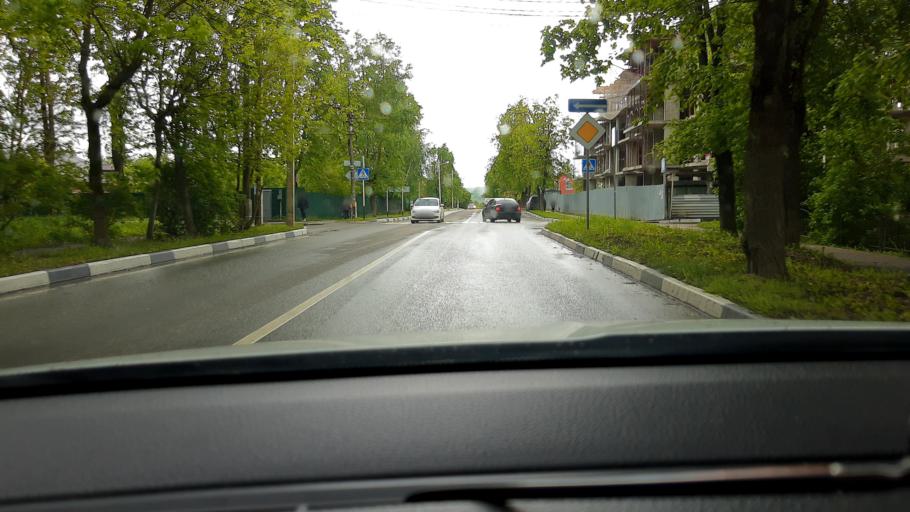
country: RU
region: Moskovskaya
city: Zvenigorod
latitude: 55.7356
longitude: 36.8612
